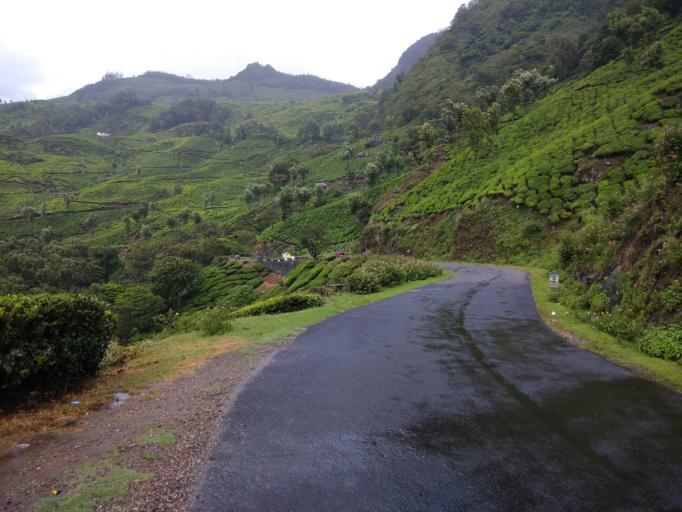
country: IN
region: Kerala
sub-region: Idukki
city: Munnar
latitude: 10.1443
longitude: 77.1069
